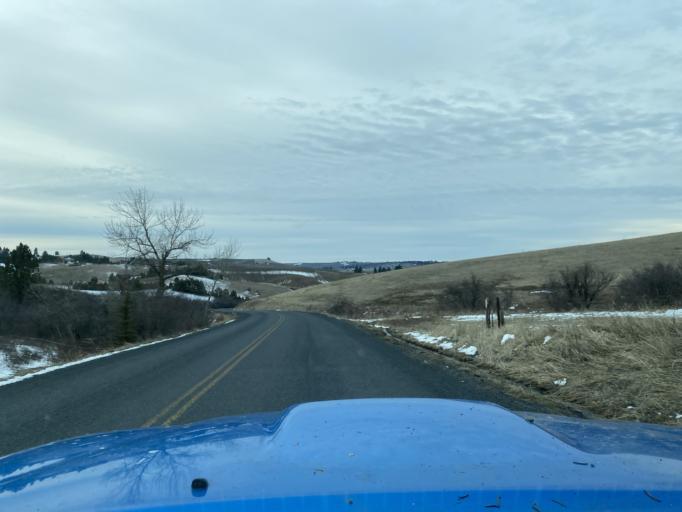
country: US
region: Idaho
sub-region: Latah County
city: Moscow
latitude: 46.7033
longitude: -116.9385
